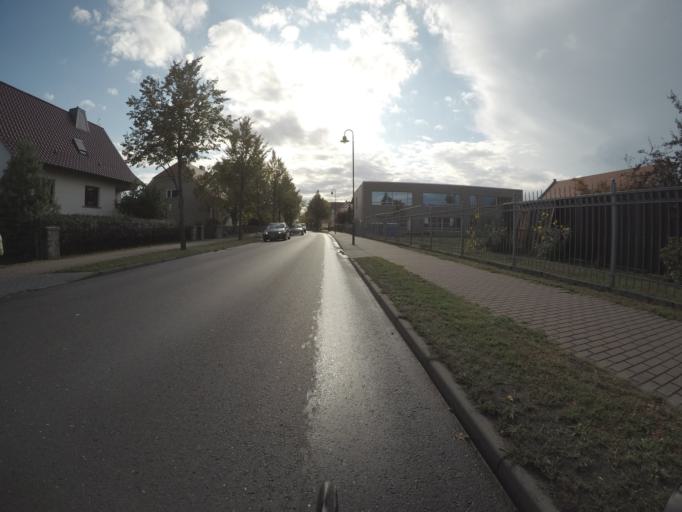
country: DE
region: Brandenburg
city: Petershagen
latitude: 52.5197
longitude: 13.7531
